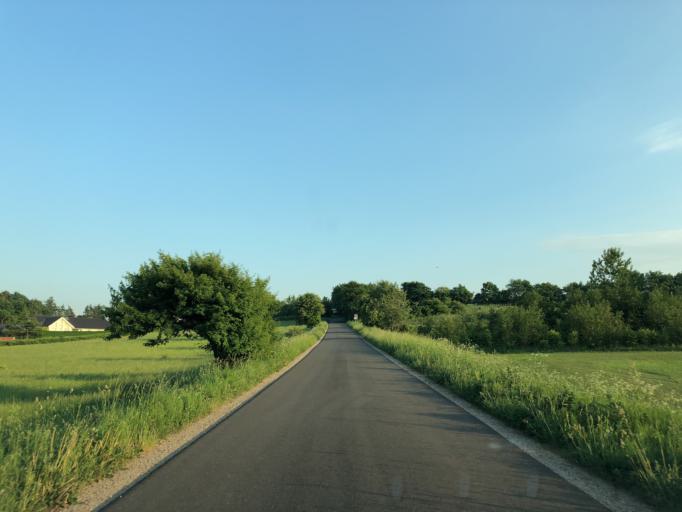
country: DK
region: Central Jutland
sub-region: Struer Kommune
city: Struer
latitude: 56.4322
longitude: 8.5054
